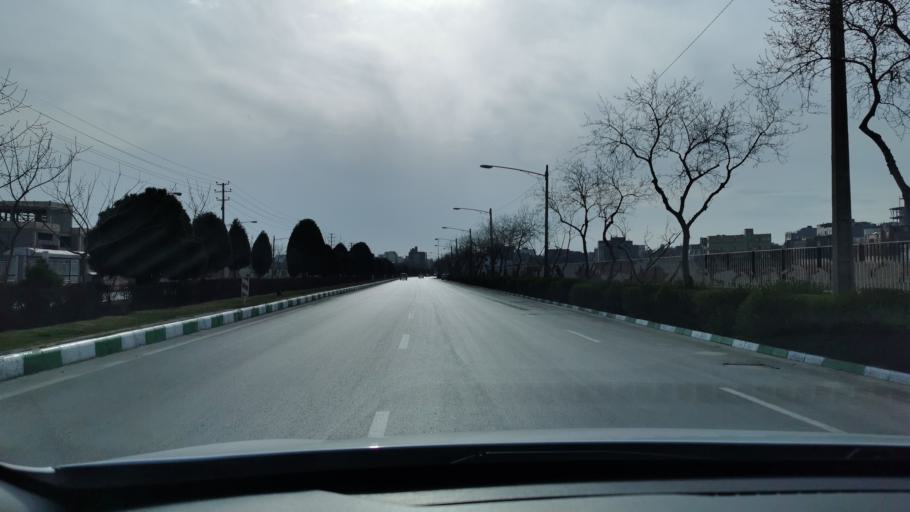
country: IR
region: Razavi Khorasan
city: Mashhad
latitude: 36.3011
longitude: 59.5198
